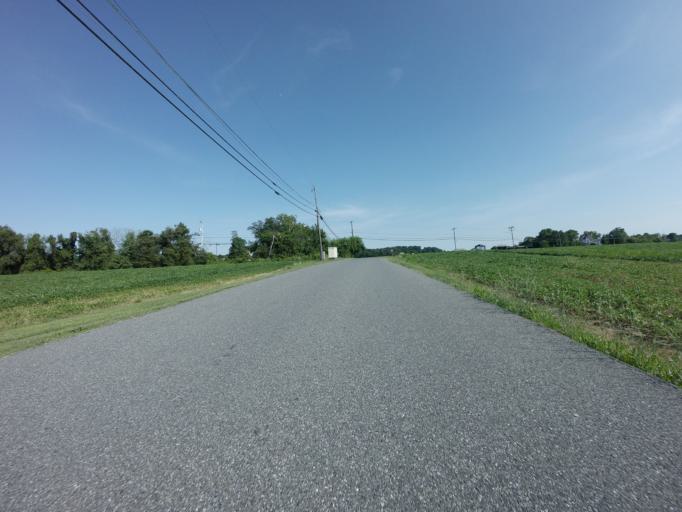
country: US
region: Maryland
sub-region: Baltimore County
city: Edgemere
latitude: 39.2163
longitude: -76.4372
